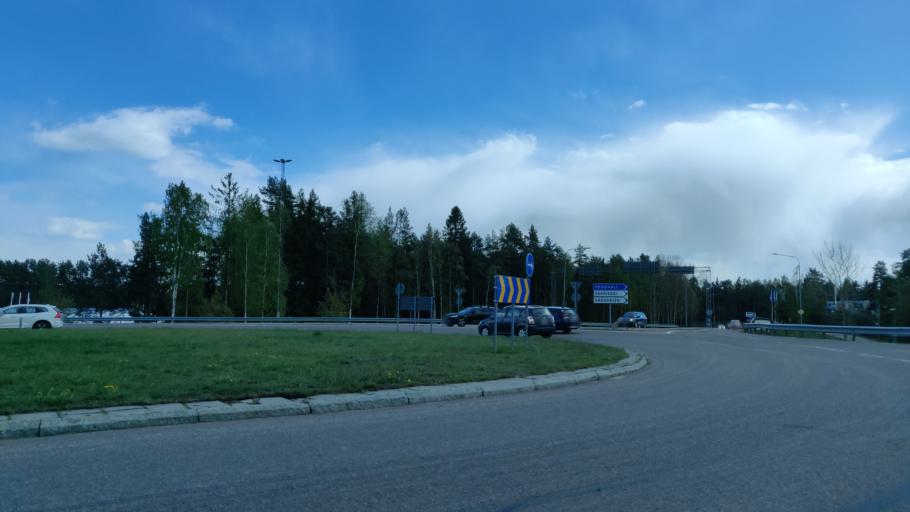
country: SE
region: Vaermland
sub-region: Hammaro Kommun
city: Skoghall
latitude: 59.3775
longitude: 13.4404
